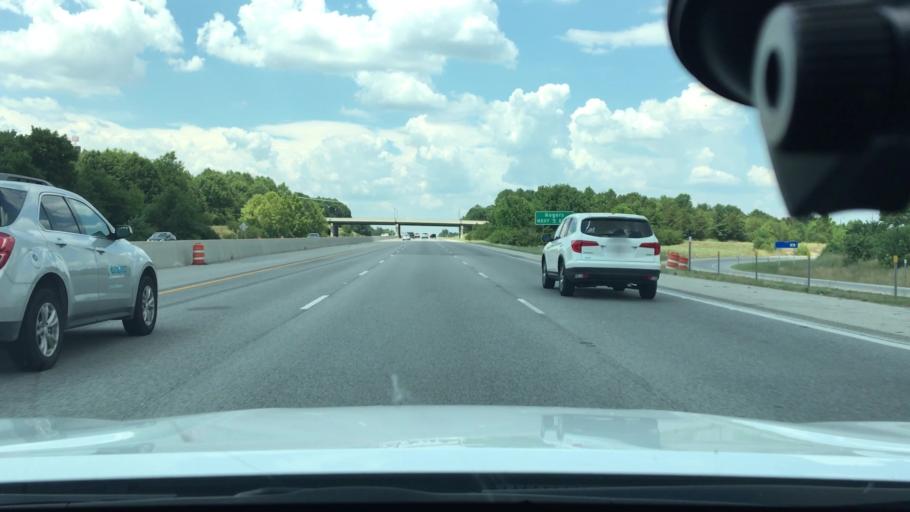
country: US
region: Arkansas
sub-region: Benton County
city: Lowell
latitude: 36.2512
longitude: -94.1504
